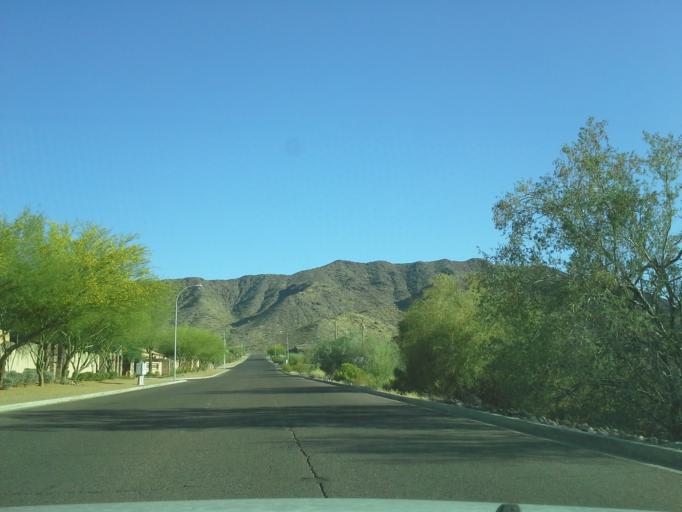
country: US
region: Arizona
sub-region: Maricopa County
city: Laveen
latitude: 33.3576
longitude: -112.1006
